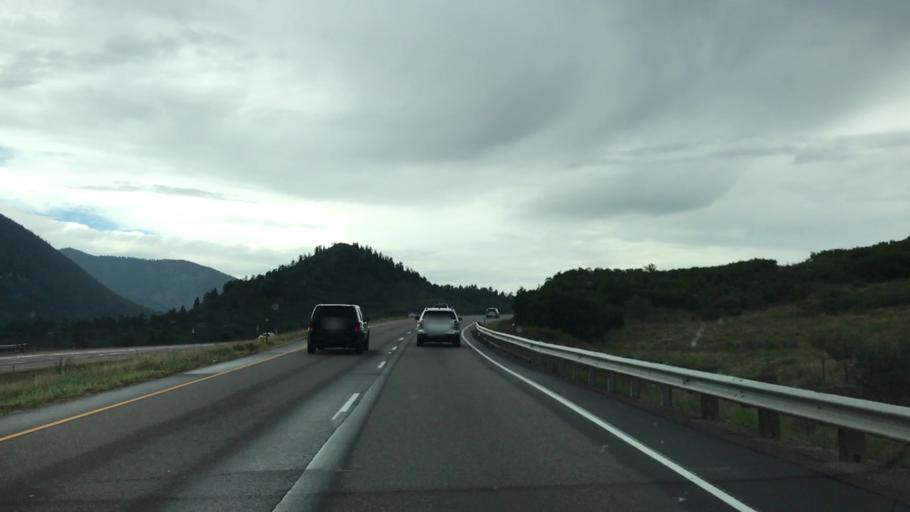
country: US
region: Colorado
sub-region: El Paso County
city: Cascade-Chipita Park
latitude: 38.9248
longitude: -104.9953
